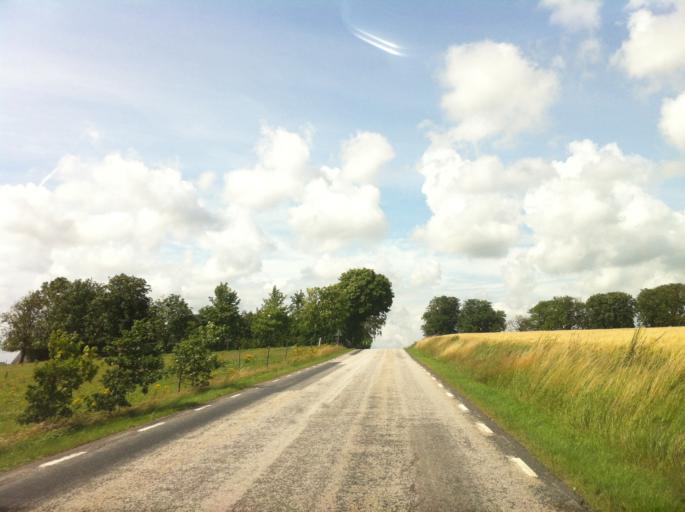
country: SE
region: Skane
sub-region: Trelleborgs Kommun
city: Anderslov
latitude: 55.5030
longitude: 13.3988
